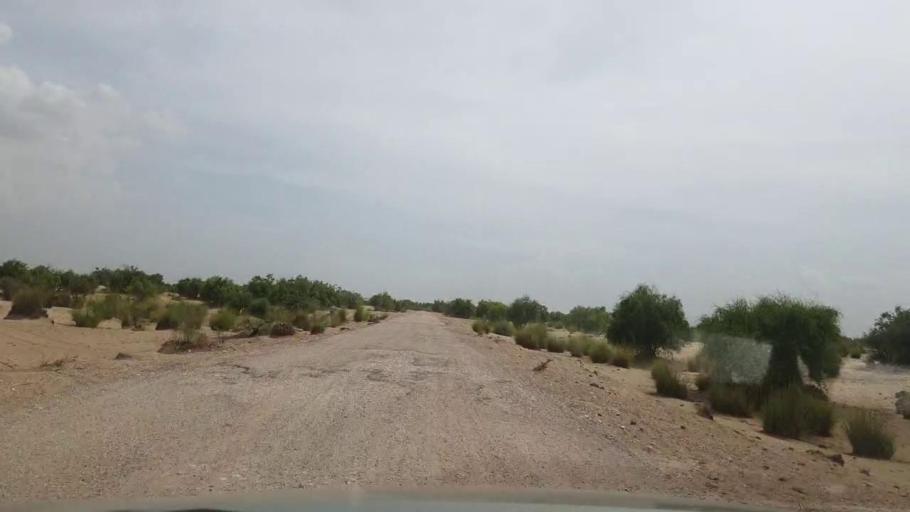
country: PK
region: Sindh
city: Bozdar
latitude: 27.0955
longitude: 69.0166
